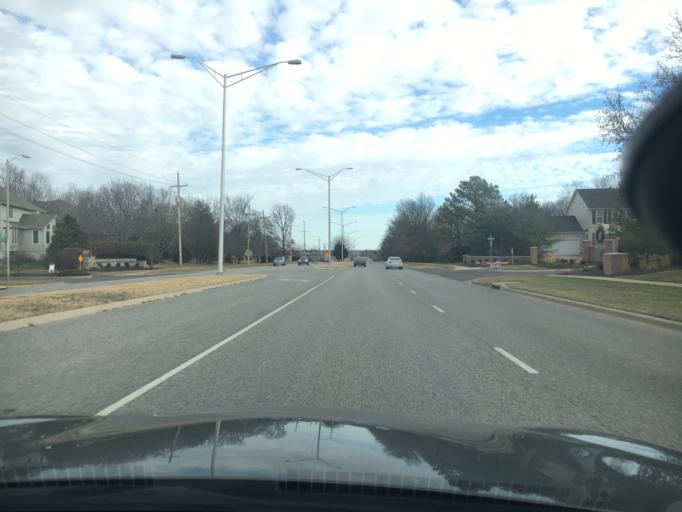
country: US
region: Kansas
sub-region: Johnson County
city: Leawood
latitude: 38.8546
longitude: -94.6557
